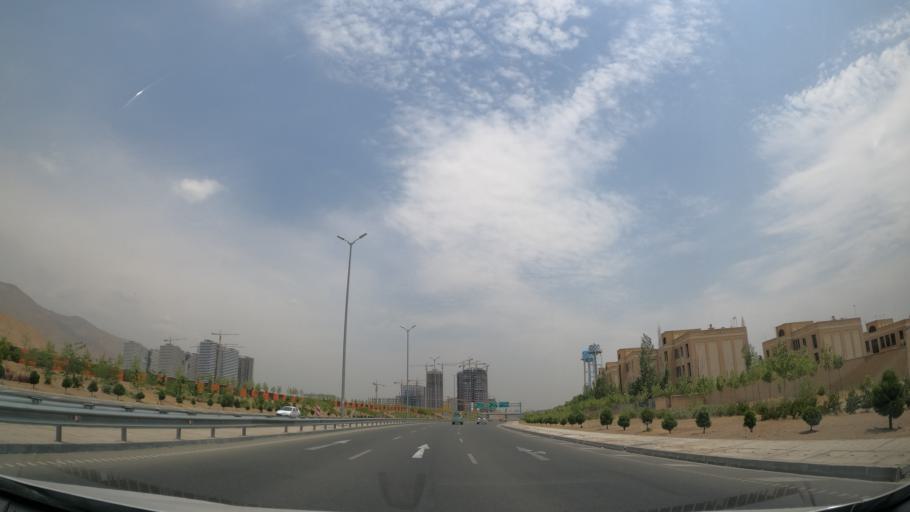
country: IR
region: Tehran
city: Shahr-e Qods
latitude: 35.7514
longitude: 51.1681
